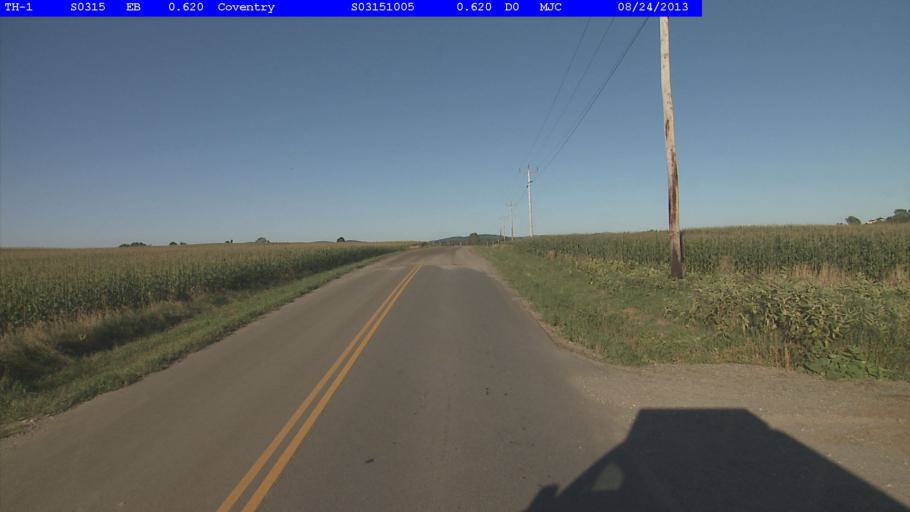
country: US
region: Vermont
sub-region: Orleans County
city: Newport
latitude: 44.8669
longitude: -72.2486
